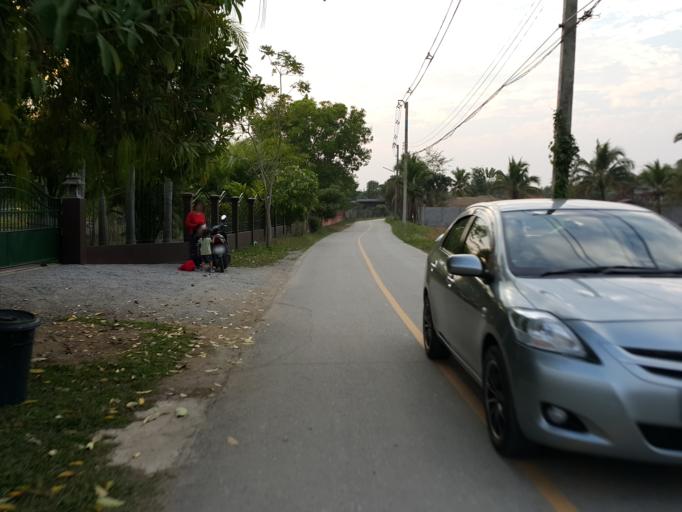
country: TH
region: Chiang Mai
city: San Sai
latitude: 18.8946
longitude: 99.1334
